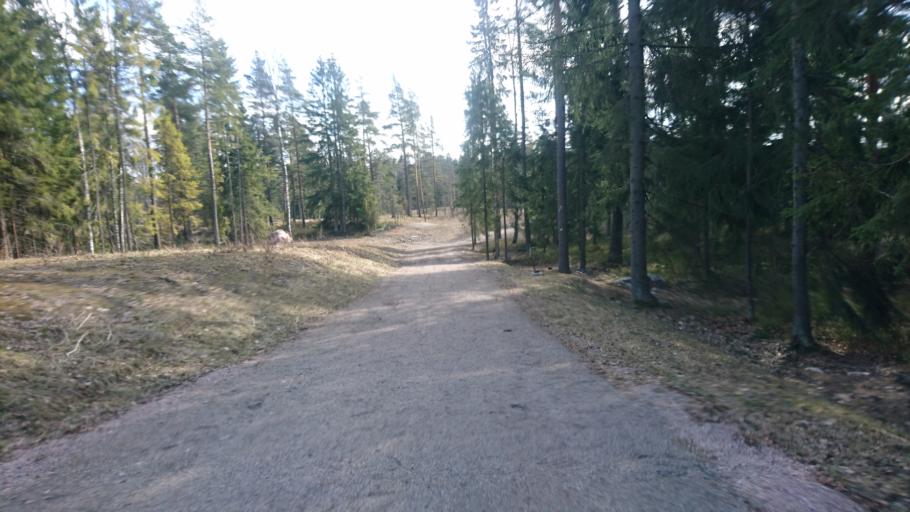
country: FI
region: Uusimaa
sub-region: Helsinki
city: Kauniainen
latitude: 60.1997
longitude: 24.7253
